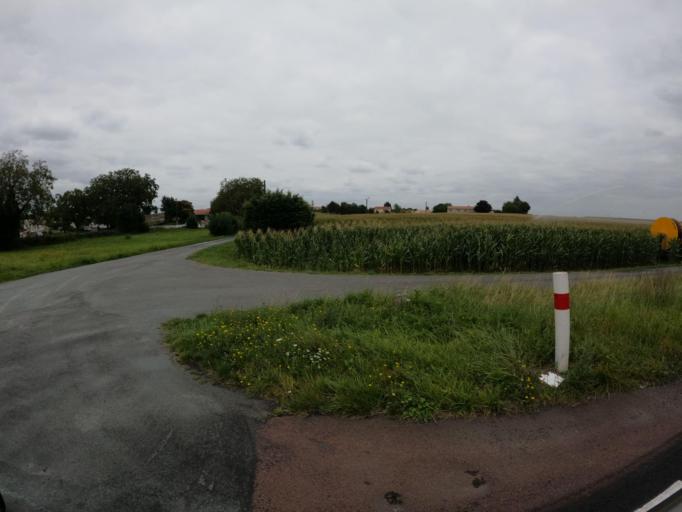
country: FR
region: Pays de la Loire
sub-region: Departement de la Vendee
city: Benet
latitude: 46.3959
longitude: -0.6514
